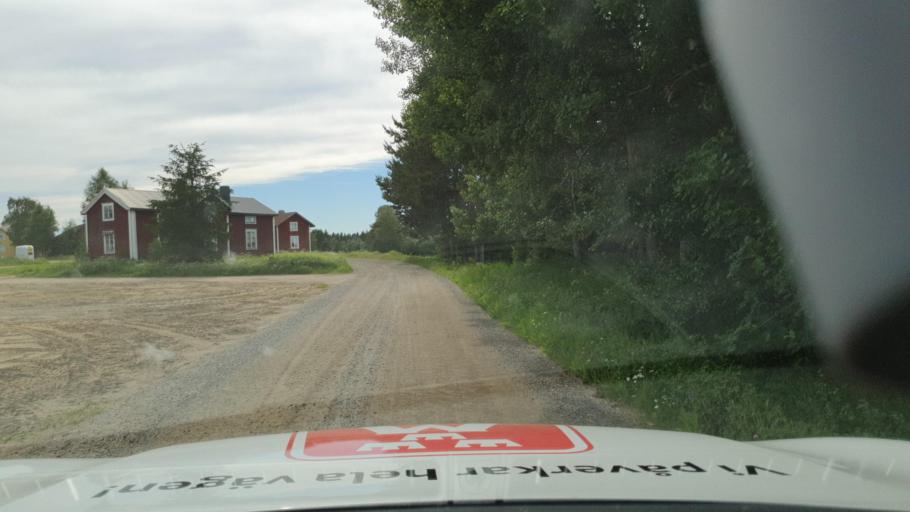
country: SE
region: Vaesterbotten
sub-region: Robertsfors Kommun
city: Robertsfors
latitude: 64.3831
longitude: 21.0377
